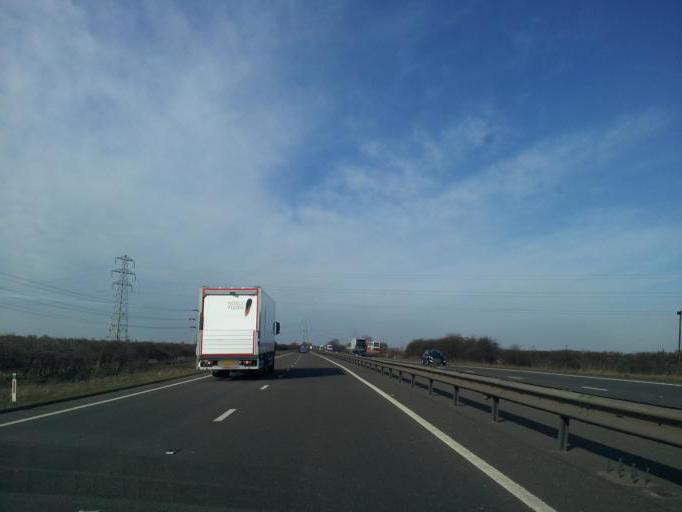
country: GB
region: England
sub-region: Lincolnshire
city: Long Bennington
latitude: 53.0046
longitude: -0.7630
